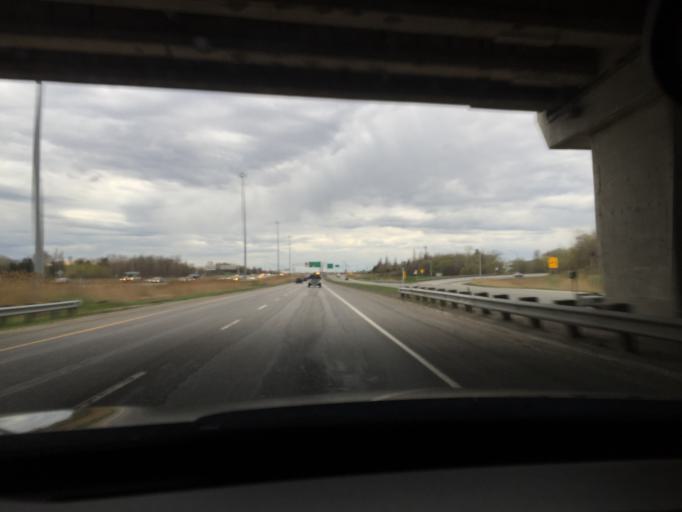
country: CA
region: Quebec
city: L'Ancienne-Lorette
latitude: 46.8247
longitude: -71.2987
